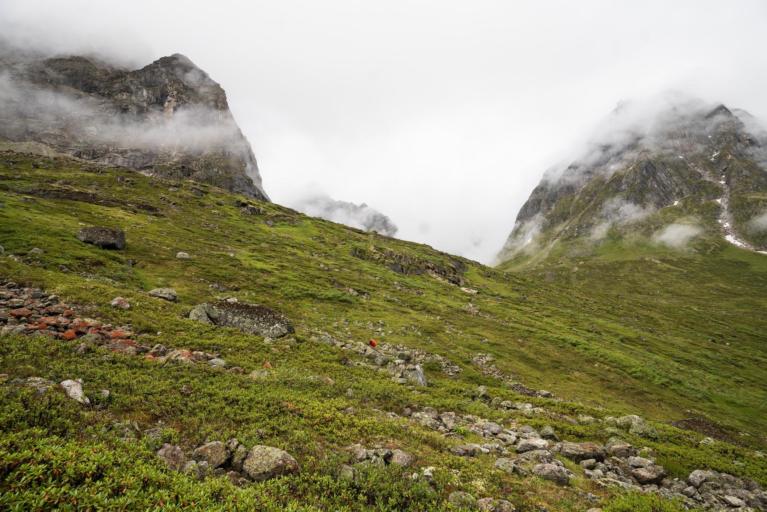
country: RU
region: Transbaikal Territory
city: Chara
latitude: 56.8753
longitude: 117.4257
